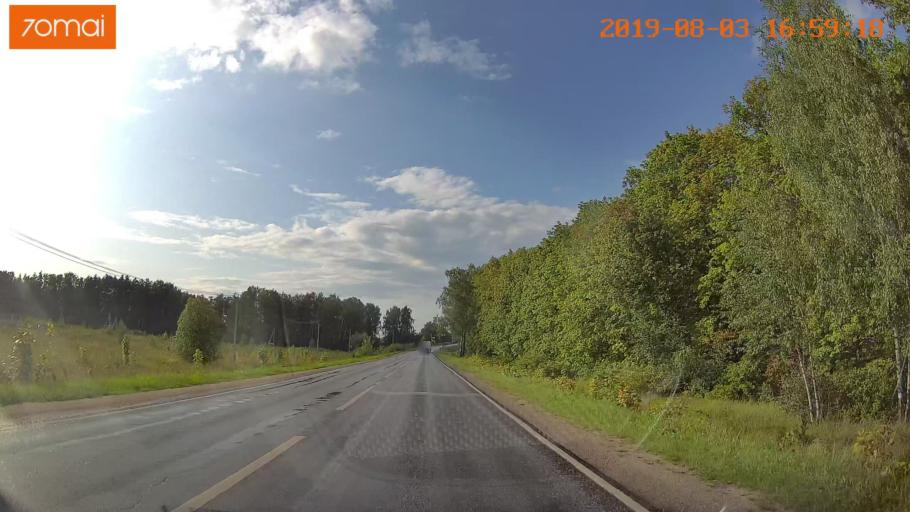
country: RU
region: Moskovskaya
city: Voskresensk
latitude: 55.3287
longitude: 38.6255
